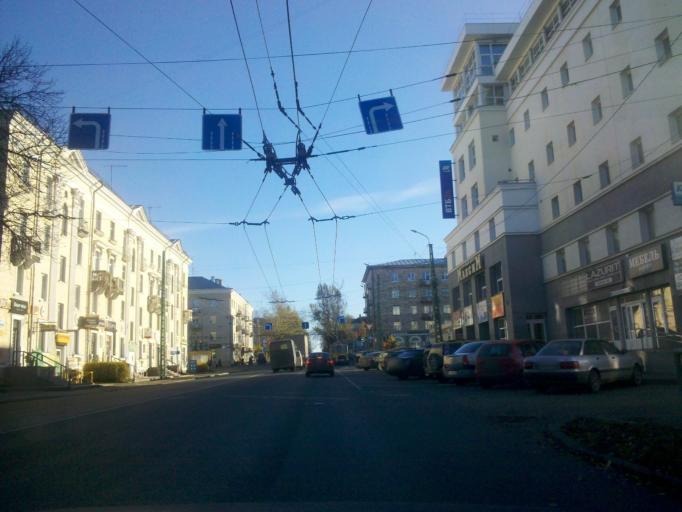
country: RU
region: Republic of Karelia
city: Petrozavodsk
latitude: 61.7929
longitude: 34.3682
